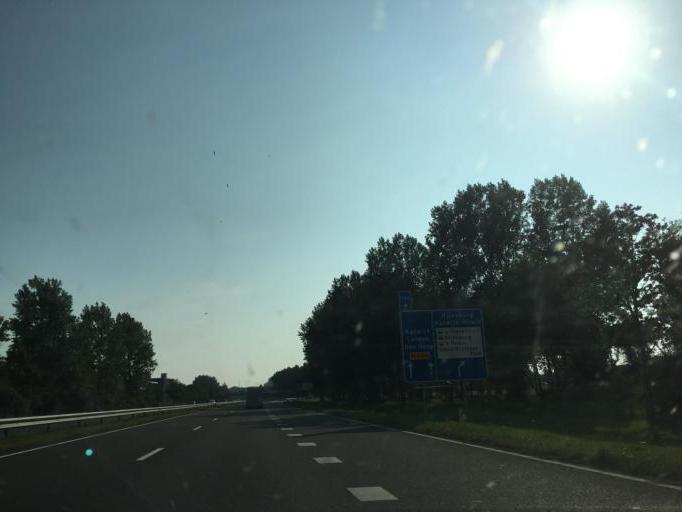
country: NL
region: South Holland
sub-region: Gemeente Noordwijk
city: Noordwijk-Binnen
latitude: 52.2123
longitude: 4.4426
